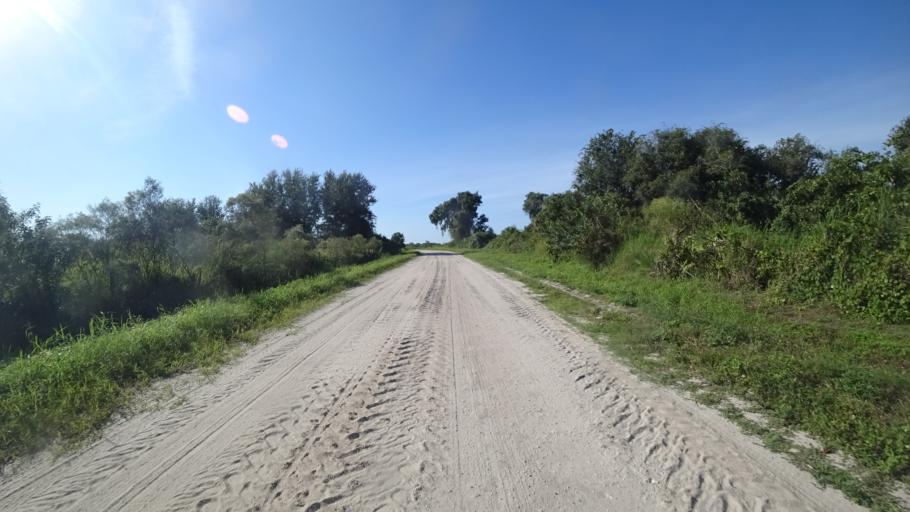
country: US
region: Florida
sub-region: Sarasota County
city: The Meadows
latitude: 27.4591
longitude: -82.3367
